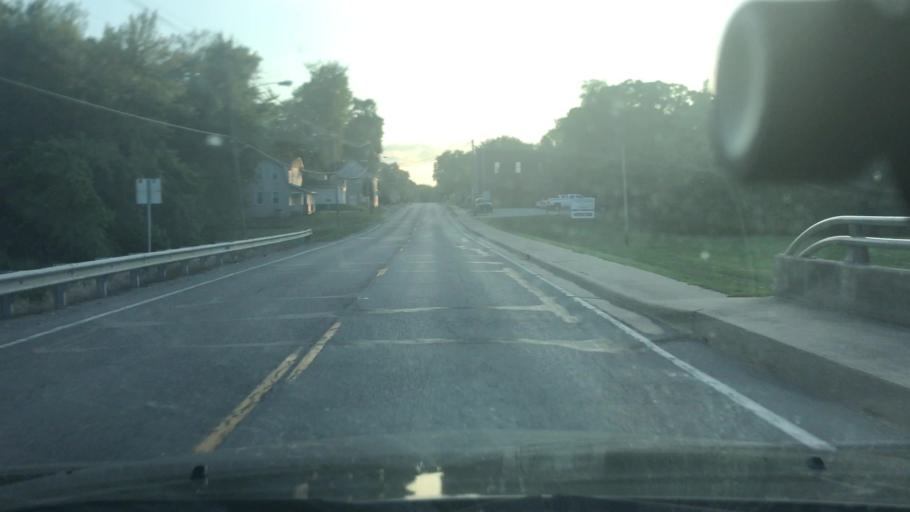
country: US
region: Illinois
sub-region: Washington County
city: Okawville
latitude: 38.4360
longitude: -89.5469
